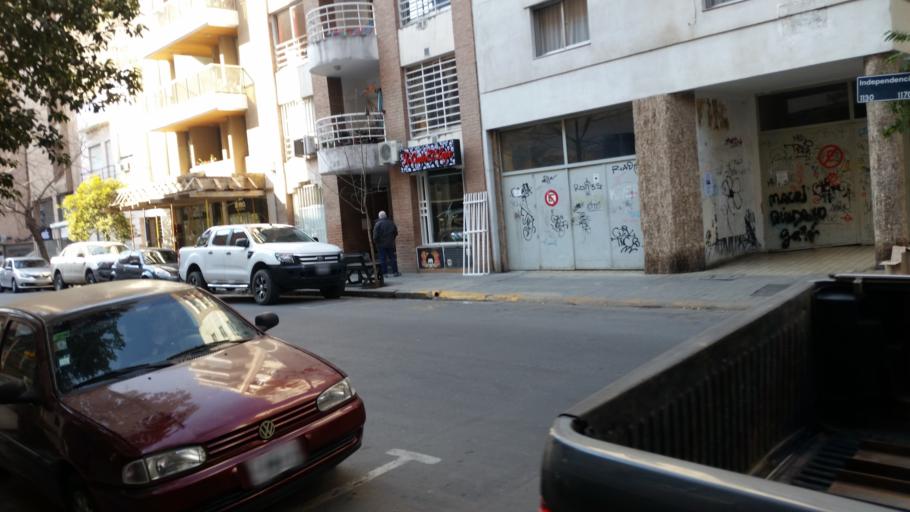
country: AR
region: Cordoba
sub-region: Departamento de Capital
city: Cordoba
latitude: -31.4295
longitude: -64.1895
